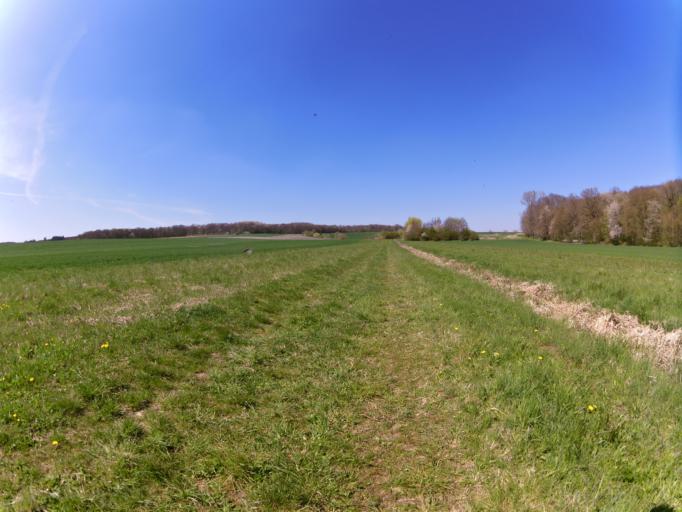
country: DE
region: Bavaria
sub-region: Regierungsbezirk Unterfranken
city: Kurnach
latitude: 49.8603
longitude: 10.0047
